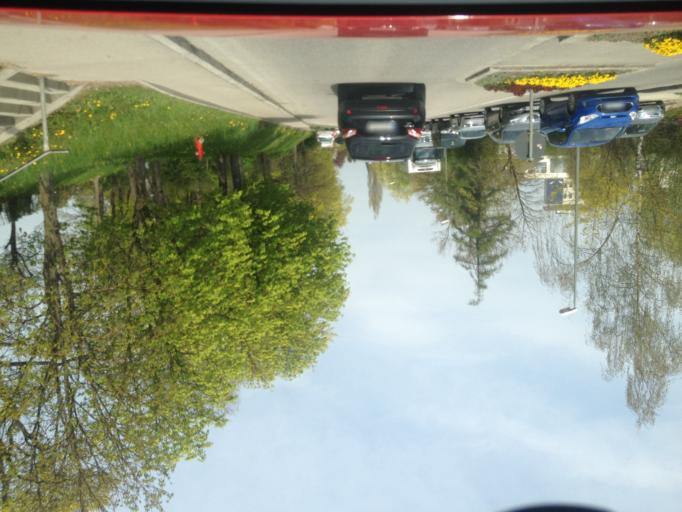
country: DE
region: Bavaria
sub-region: Upper Bavaria
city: Pfaffenhofen an der Ilm
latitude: 48.5235
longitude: 11.5112
